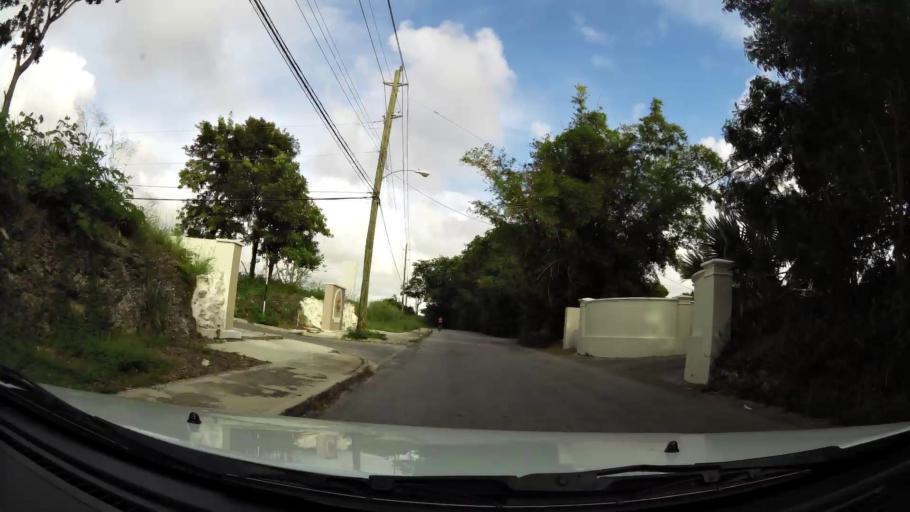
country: BB
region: Christ Church
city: Oistins
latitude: 13.0932
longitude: -59.5663
